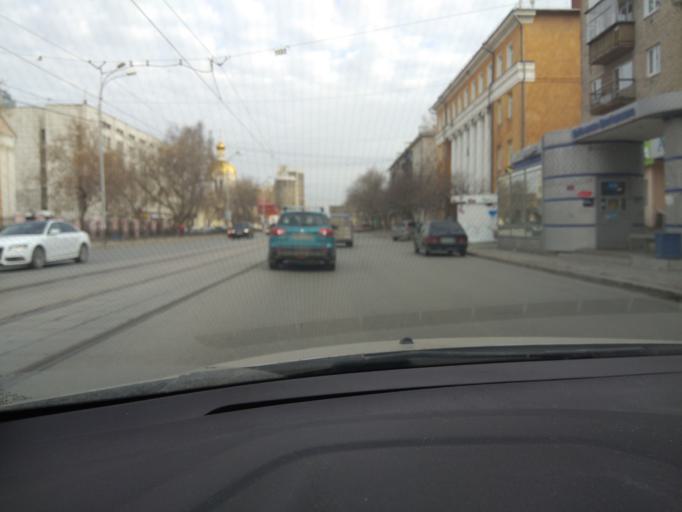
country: RU
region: Sverdlovsk
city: Yekaterinburg
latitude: 56.8304
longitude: 60.6241
